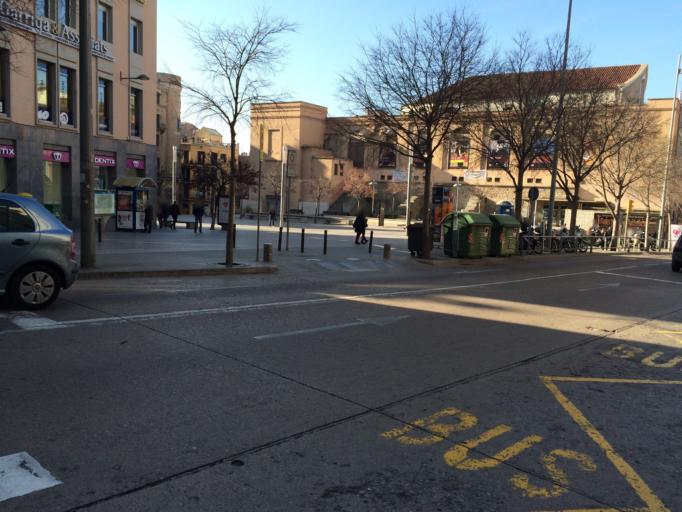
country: ES
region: Catalonia
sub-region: Provincia de Barcelona
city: Manresa
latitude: 41.7254
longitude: 1.8244
